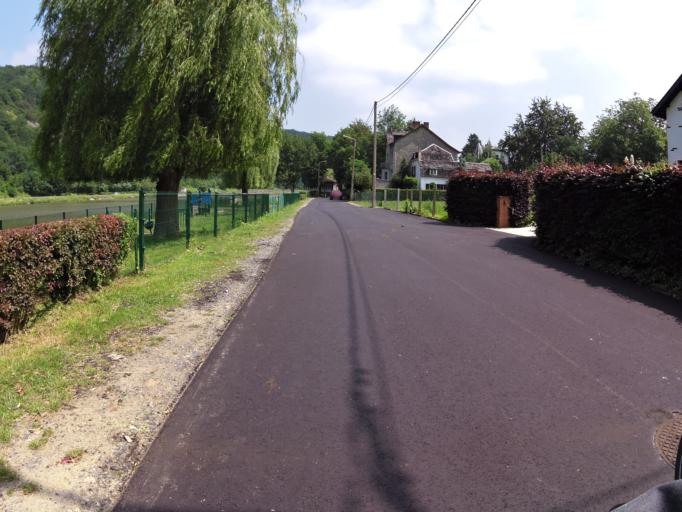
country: BE
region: Wallonia
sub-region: Province de Namur
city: Hastiere-Lavaux
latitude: 50.2162
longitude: 4.8318
